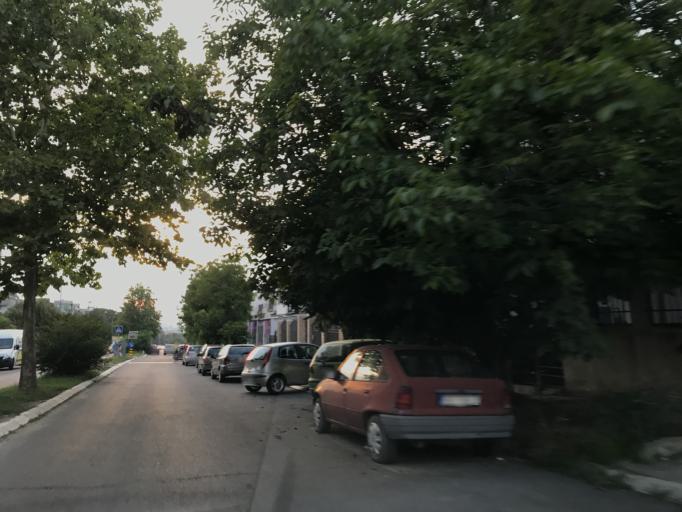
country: RS
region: Central Serbia
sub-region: Belgrade
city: Vozdovac
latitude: 44.7759
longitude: 20.5031
